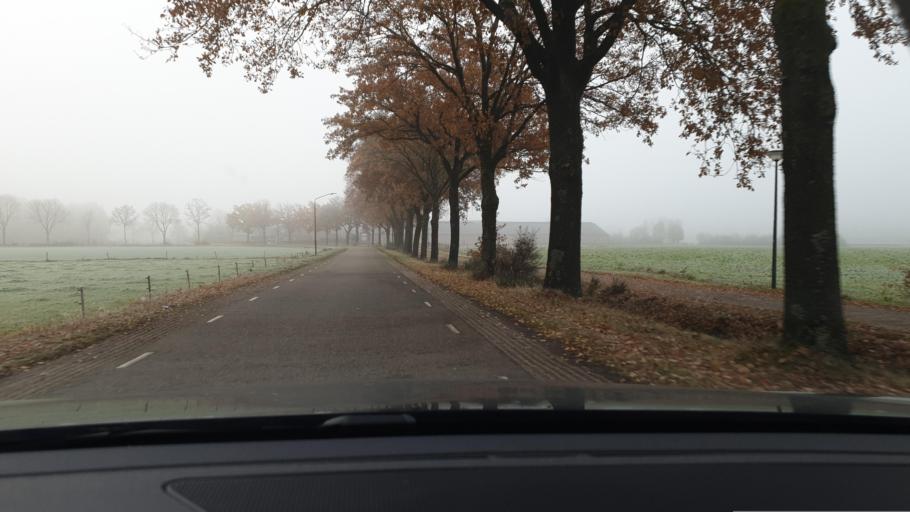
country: NL
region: North Brabant
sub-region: Gemeente Bladel en Netersel
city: Bladel
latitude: 51.3822
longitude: 5.1743
